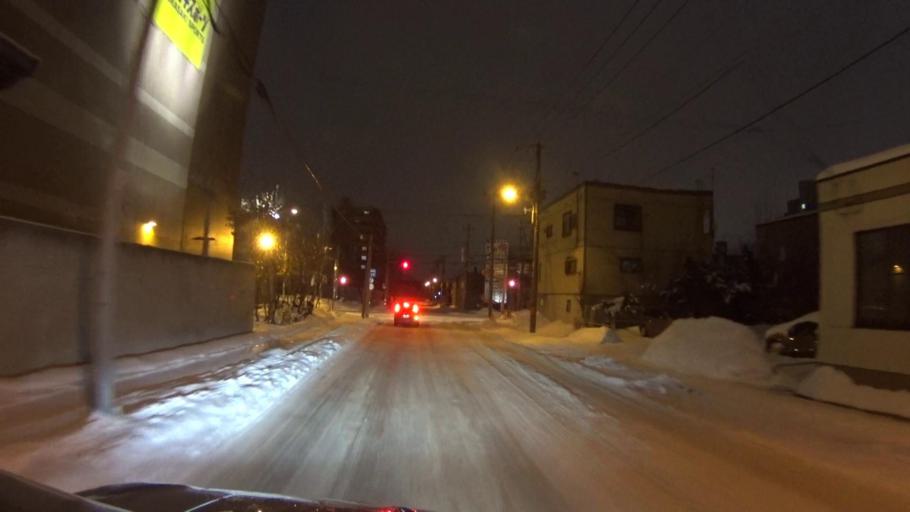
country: JP
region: Hokkaido
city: Sapporo
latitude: 43.0957
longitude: 141.2788
